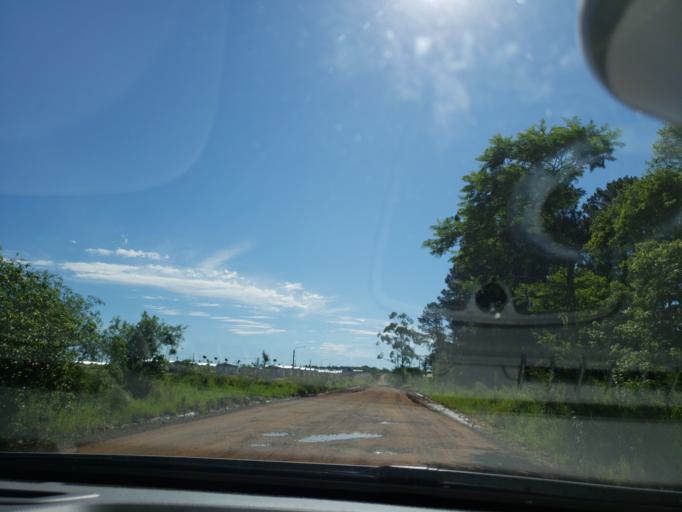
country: PY
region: Itapua
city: San Juan del Parana
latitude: -27.3911
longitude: -55.9946
